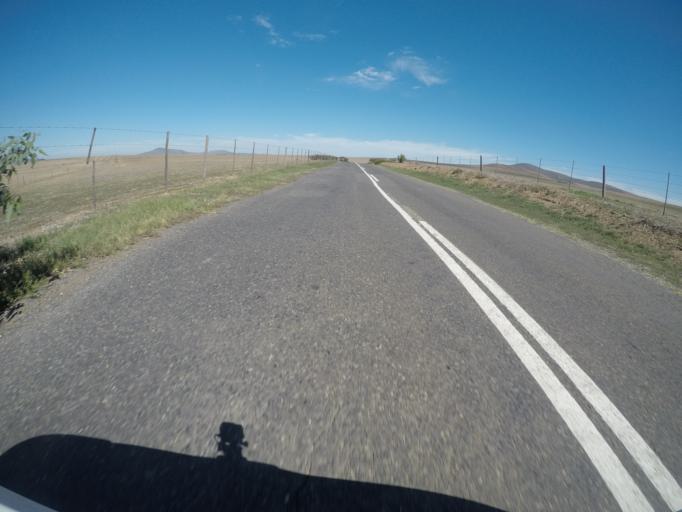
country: ZA
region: Western Cape
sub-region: City of Cape Town
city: Atlantis
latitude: -33.6930
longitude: 18.5932
